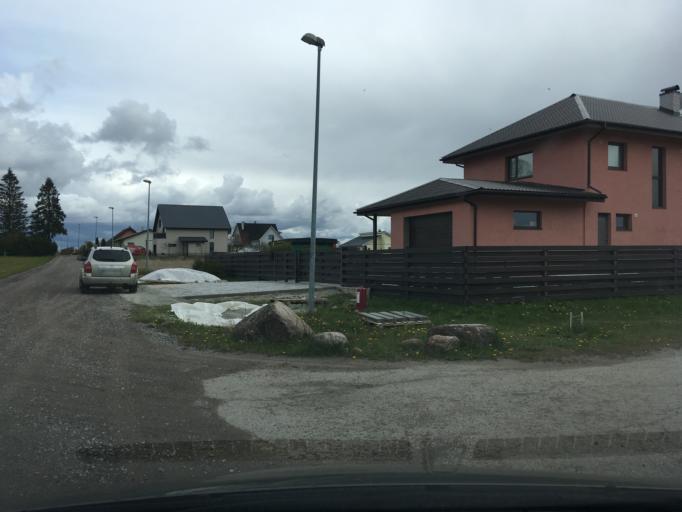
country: EE
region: Harju
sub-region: Joelaehtme vald
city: Loo
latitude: 59.4054
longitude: 24.9477
